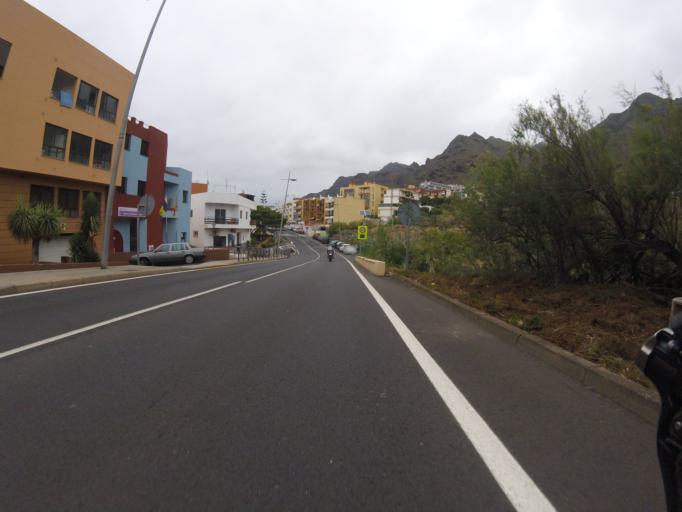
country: ES
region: Canary Islands
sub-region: Provincia de Santa Cruz de Tenerife
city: Tegueste
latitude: 28.5528
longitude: -16.3464
